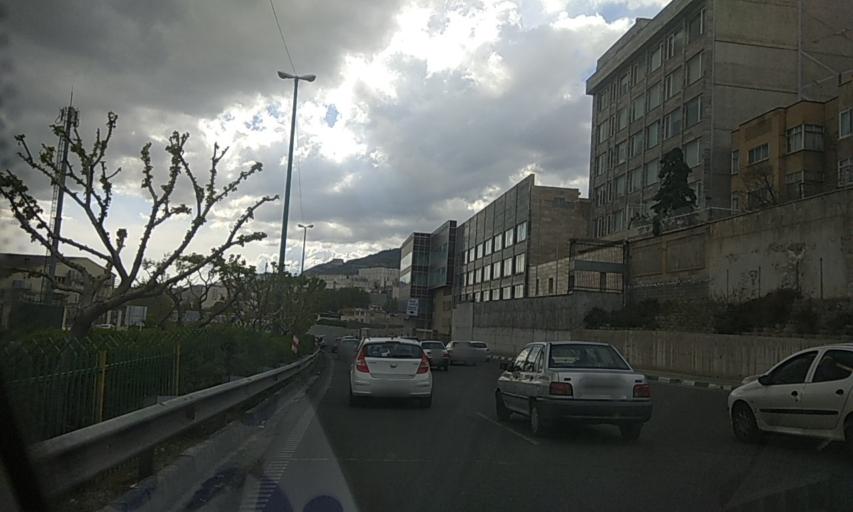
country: IR
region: Tehran
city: Tajrish
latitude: 35.7847
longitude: 51.3499
